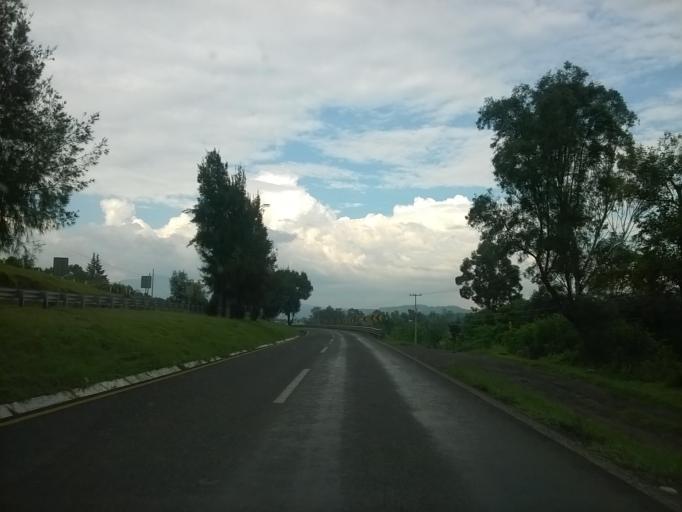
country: MX
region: Michoacan
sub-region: Huiramba
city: El Pedregal
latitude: 19.5311
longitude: -101.4776
